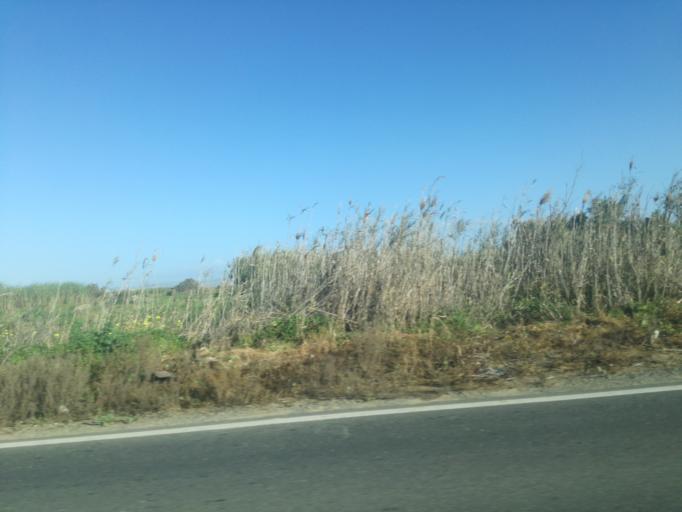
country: IT
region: Sicily
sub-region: Provincia di Caltanissetta
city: Gela
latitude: 37.0543
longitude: 14.3022
